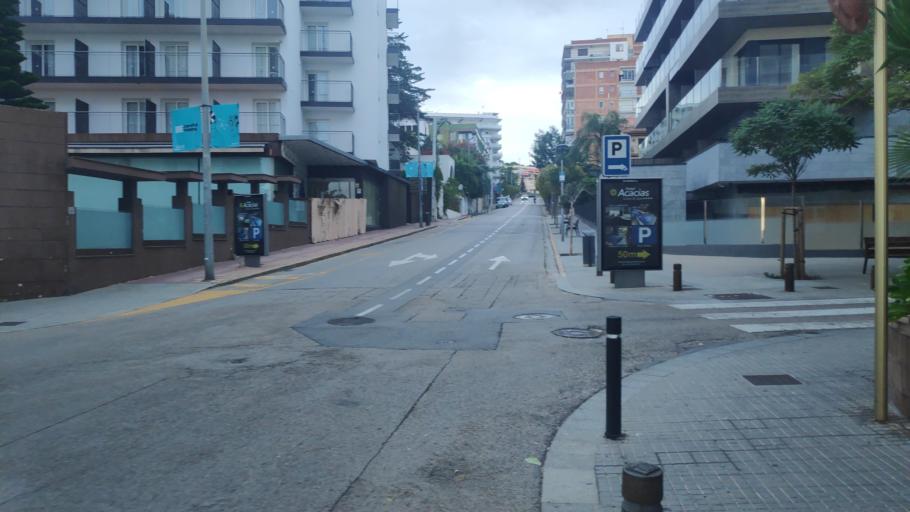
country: ES
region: Catalonia
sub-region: Provincia de Girona
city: Lloret de Mar
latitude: 41.7013
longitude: 2.8556
